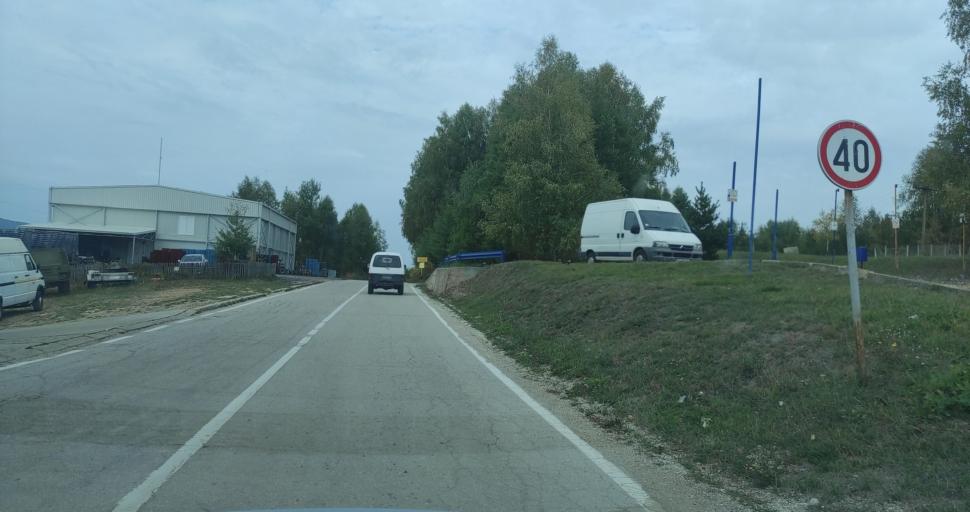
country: RS
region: Central Serbia
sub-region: Jablanicki Okrug
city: Crna Trava
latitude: 42.6697
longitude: 22.3190
